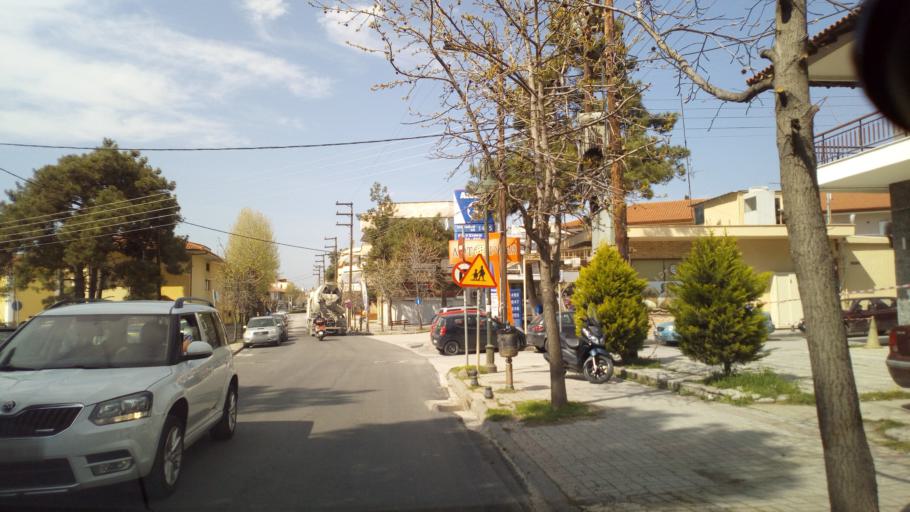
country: GR
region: Central Macedonia
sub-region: Nomos Thessalonikis
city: Thermi
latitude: 40.5494
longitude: 23.0229
